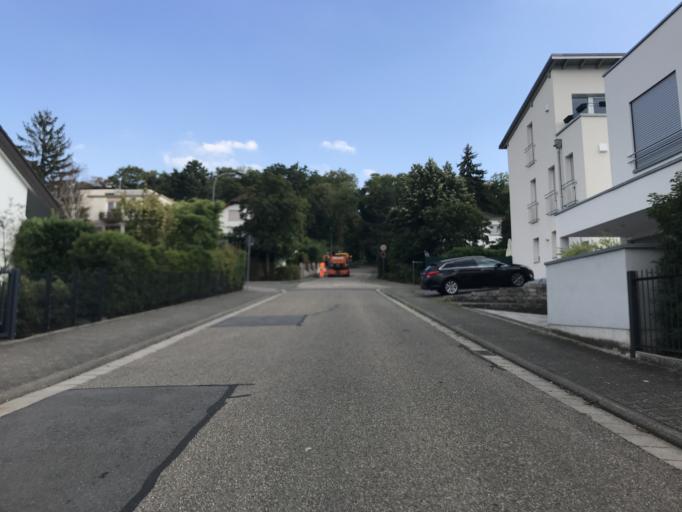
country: DE
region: Rheinland-Pfalz
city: Budenheim
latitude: 50.0194
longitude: 8.1715
